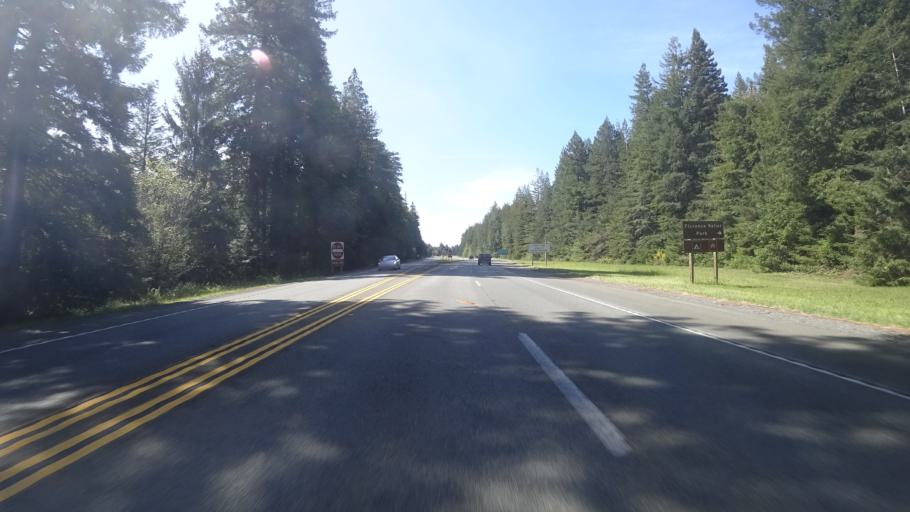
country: US
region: California
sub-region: Del Norte County
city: Bertsch-Oceanview
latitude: 41.8114
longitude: -124.1469
